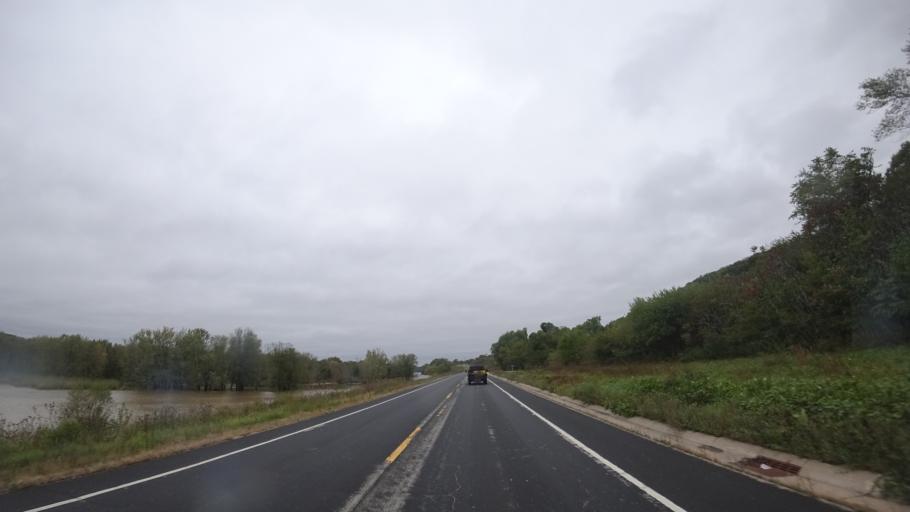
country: US
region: Wisconsin
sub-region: Grant County
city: Boscobel
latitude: 43.1182
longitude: -90.7863
